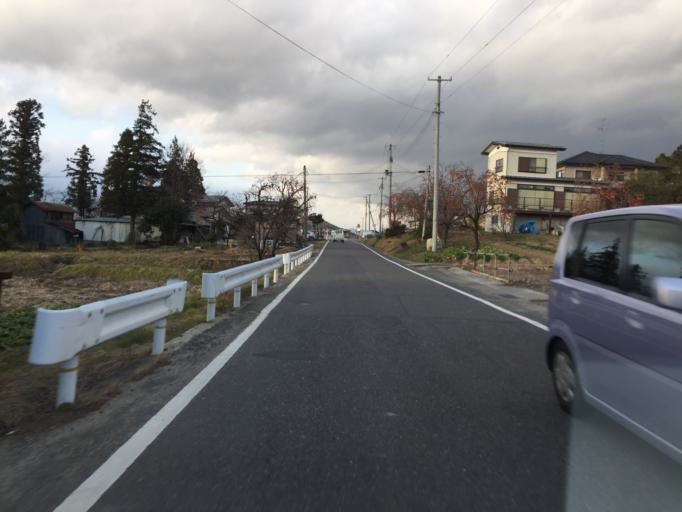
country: JP
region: Fukushima
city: Motomiya
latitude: 37.5085
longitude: 140.4113
